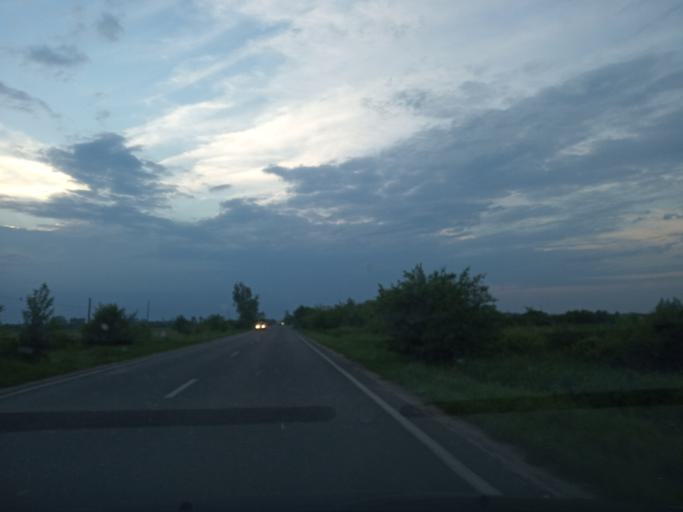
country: RO
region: Timis
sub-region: Comuna Denta
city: Denta
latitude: 45.3692
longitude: 21.2407
